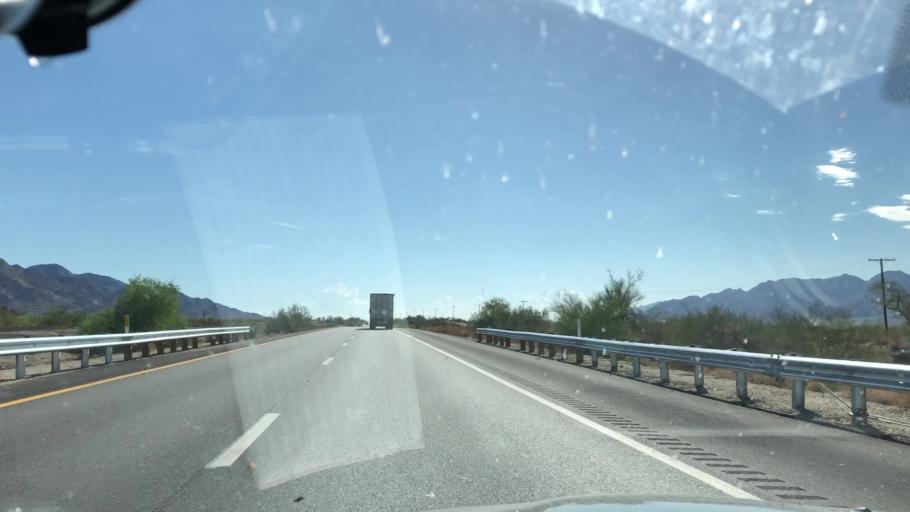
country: US
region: California
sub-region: Imperial County
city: Niland
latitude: 33.7096
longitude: -115.4198
